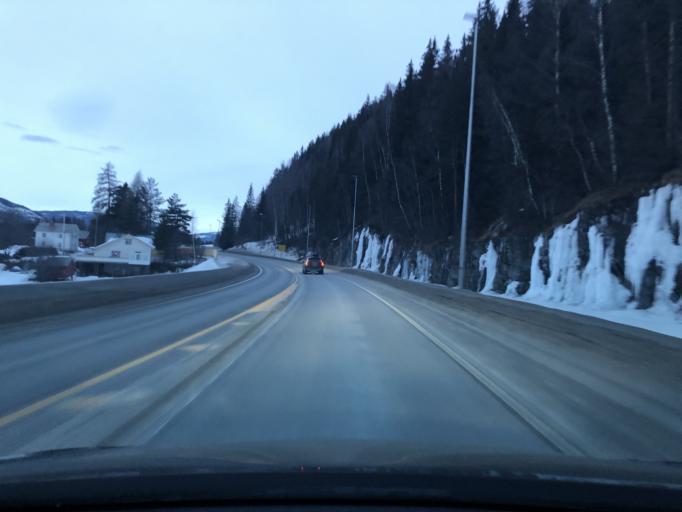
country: NO
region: Oppland
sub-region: Sor-Aurdal
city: Bagn
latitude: 60.8974
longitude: 9.4581
